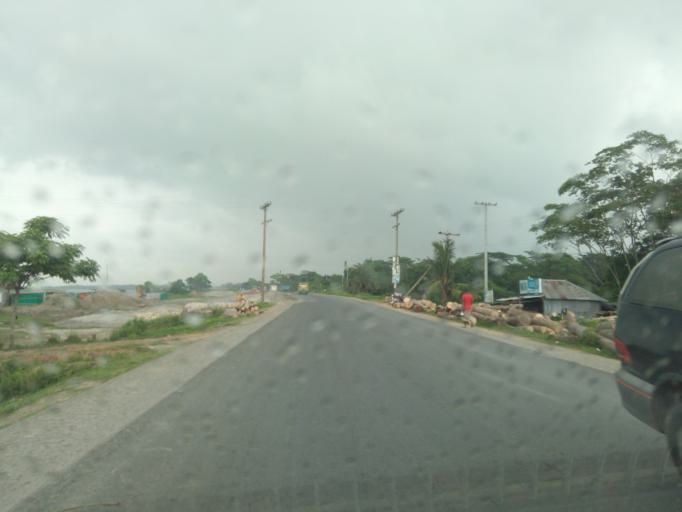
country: BD
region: Dhaka
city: Char Bhadrasan
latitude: 23.3693
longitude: 90.0715
